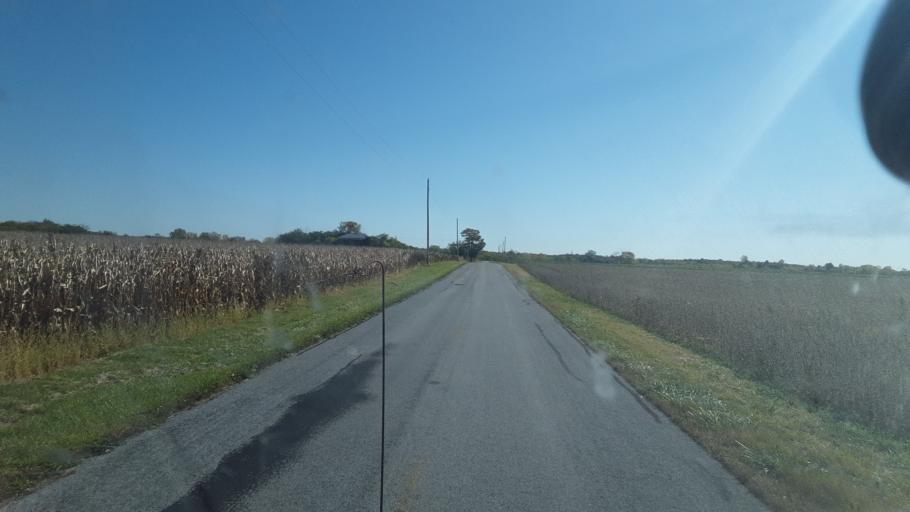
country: US
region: Ohio
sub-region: Hardin County
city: Forest
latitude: 40.6872
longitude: -83.4267
